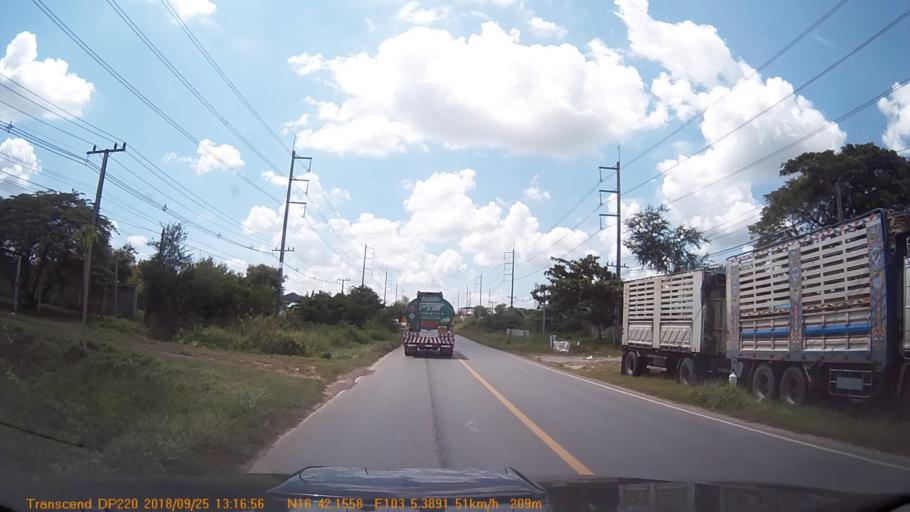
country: TH
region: Khon Kaen
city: Kranuan
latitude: 16.7025
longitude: 103.0901
